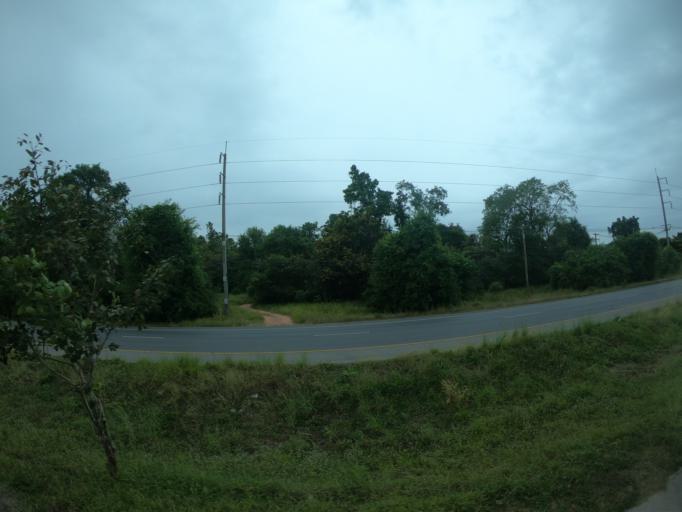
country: TH
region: Maha Sarakham
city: Maha Sarakham
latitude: 16.1282
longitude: 103.2269
